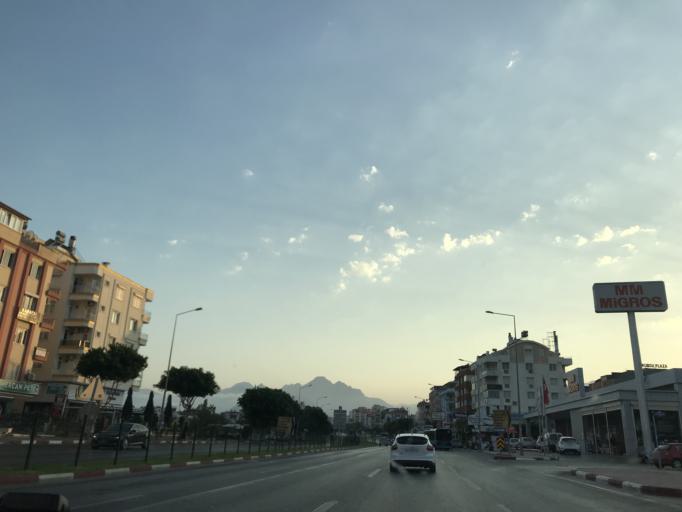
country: TR
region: Antalya
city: Antalya
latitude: 36.8792
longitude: 30.6491
